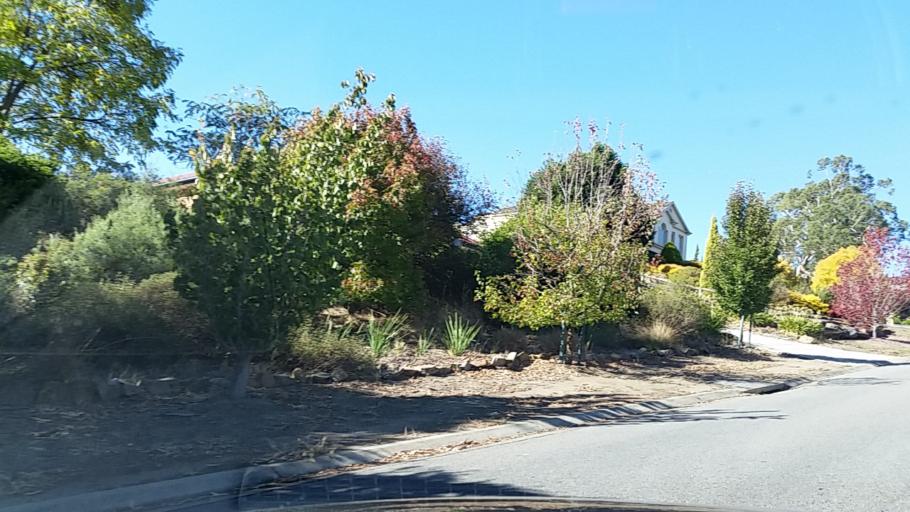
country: AU
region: South Australia
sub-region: Mount Barker
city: Mount Barker
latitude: -35.0617
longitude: 138.8769
